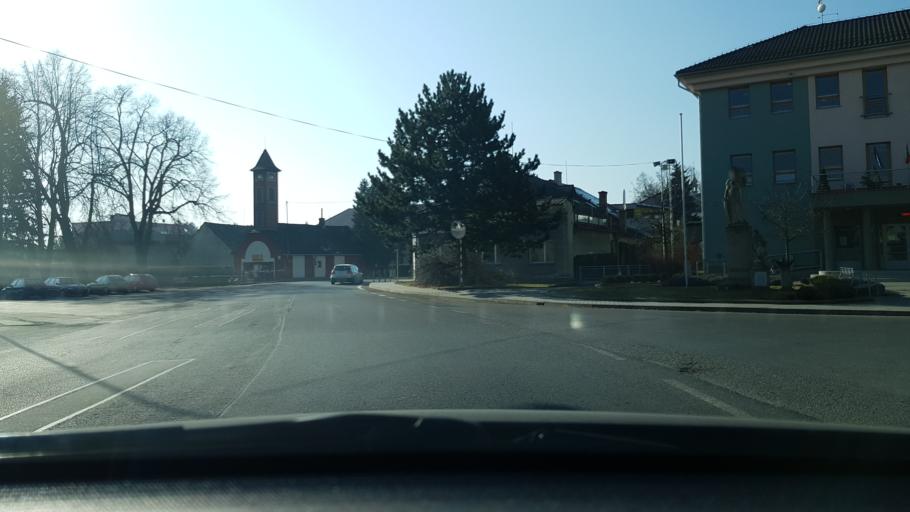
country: CZ
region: Olomoucky
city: Postrelmov
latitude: 49.9077
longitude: 16.9120
